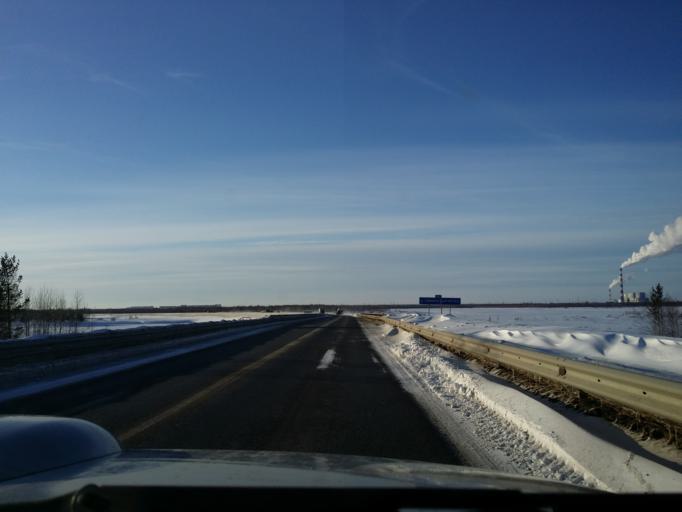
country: RU
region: Khanty-Mansiyskiy Avtonomnyy Okrug
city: Izluchinsk
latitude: 60.9337
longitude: 76.9830
